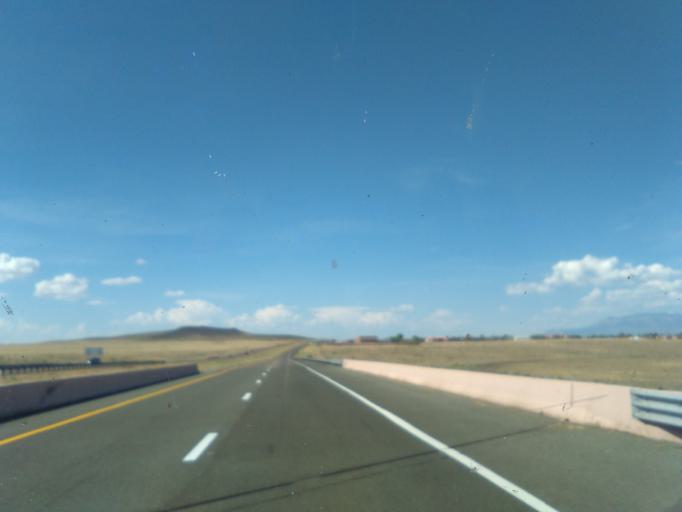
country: US
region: New Mexico
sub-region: Valencia County
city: Bosque Farms
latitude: 34.8894
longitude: -106.7272
